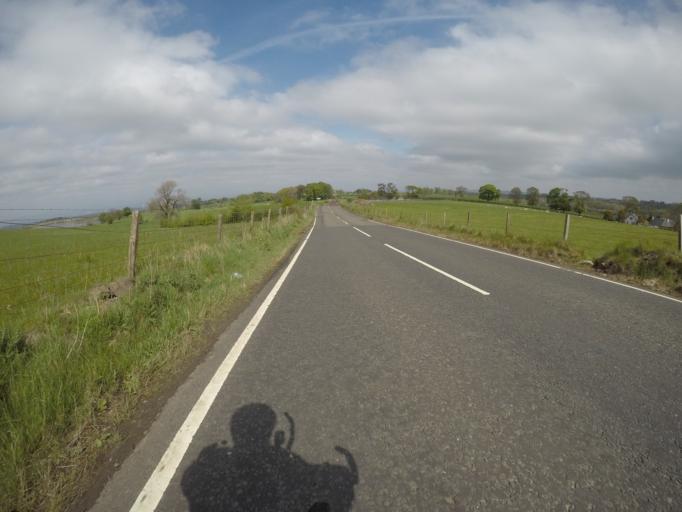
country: GB
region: Scotland
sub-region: East Renfrewshire
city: Newton Mearns
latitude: 55.7736
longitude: -4.3665
